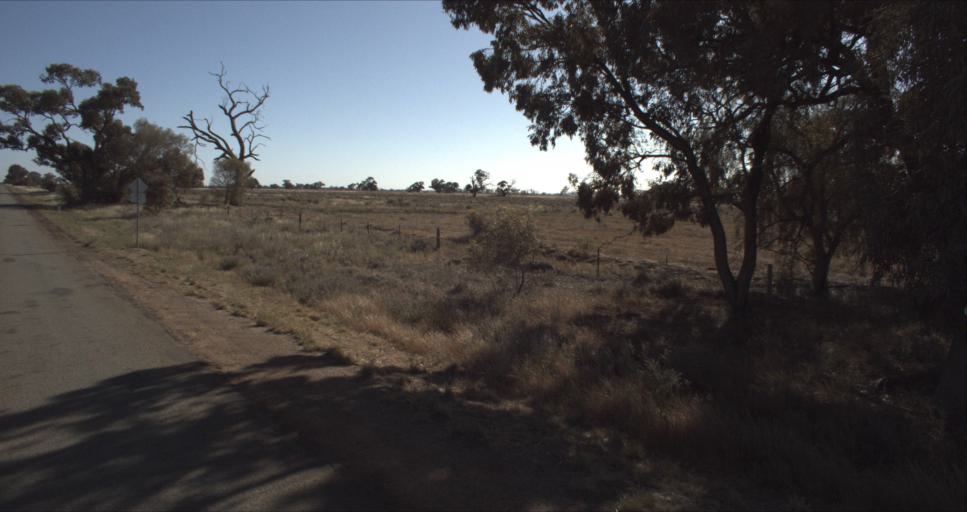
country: AU
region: New South Wales
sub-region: Leeton
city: Leeton
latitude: -34.6042
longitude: 146.2571
